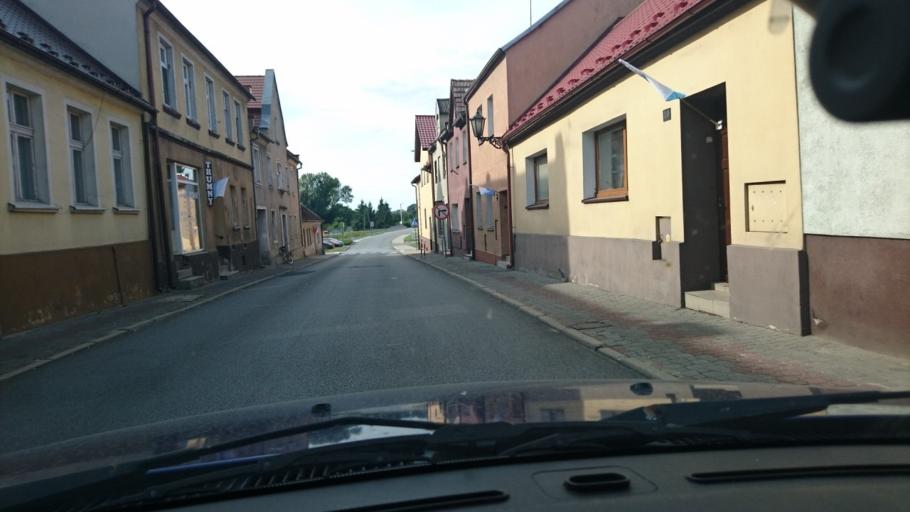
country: PL
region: Greater Poland Voivodeship
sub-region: Powiat rawicki
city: Jutrosin
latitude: 51.6543
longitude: 17.1683
